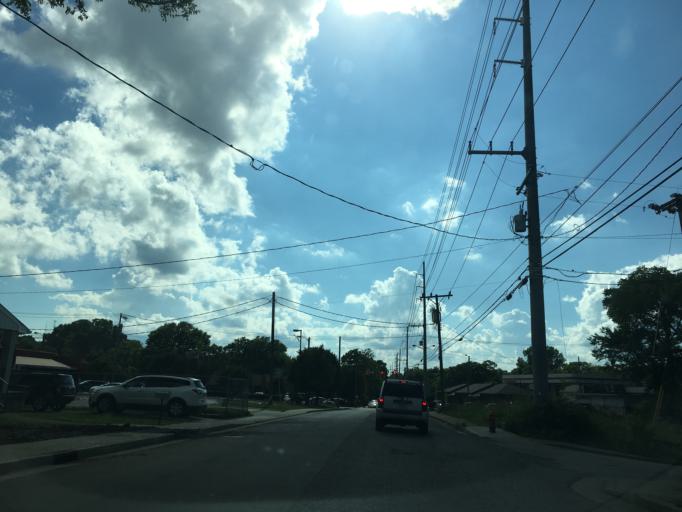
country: US
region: Tennessee
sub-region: Davidson County
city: Nashville
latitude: 36.1587
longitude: -86.8174
